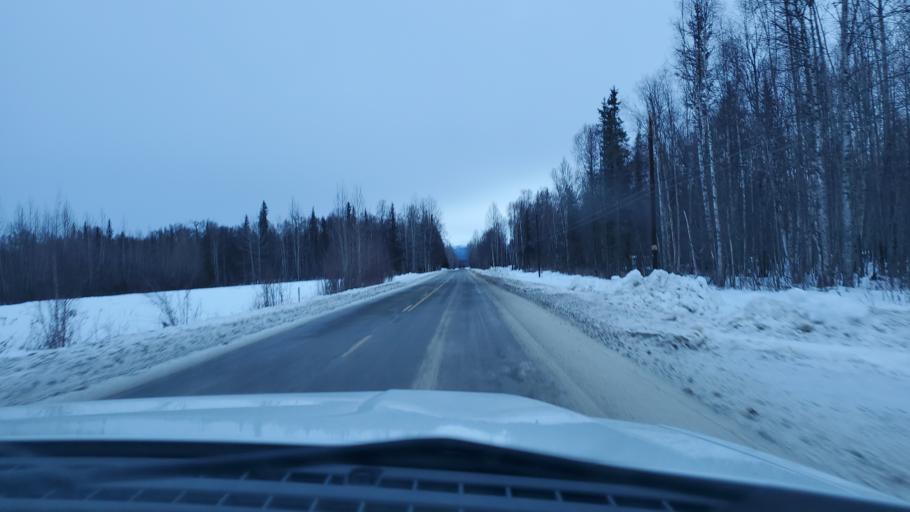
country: US
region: Alaska
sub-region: Matanuska-Susitna Borough
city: Y
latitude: 62.3163
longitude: -150.2532
